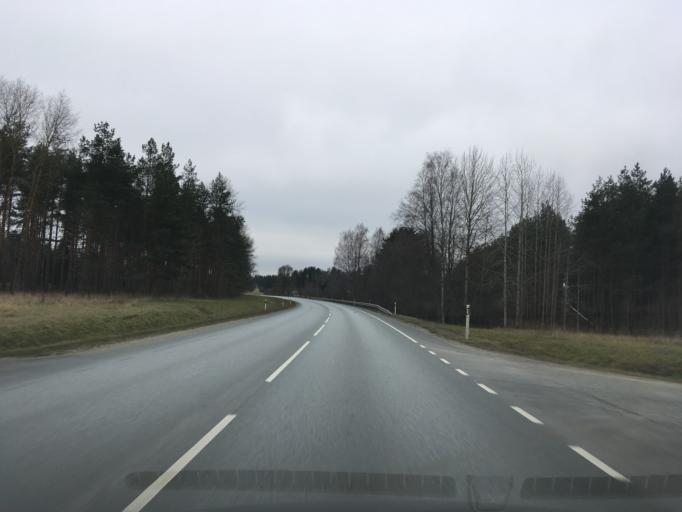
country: EE
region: Laeaene-Virumaa
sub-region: Viru-Nigula vald
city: Kunda
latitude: 59.4088
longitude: 26.6408
